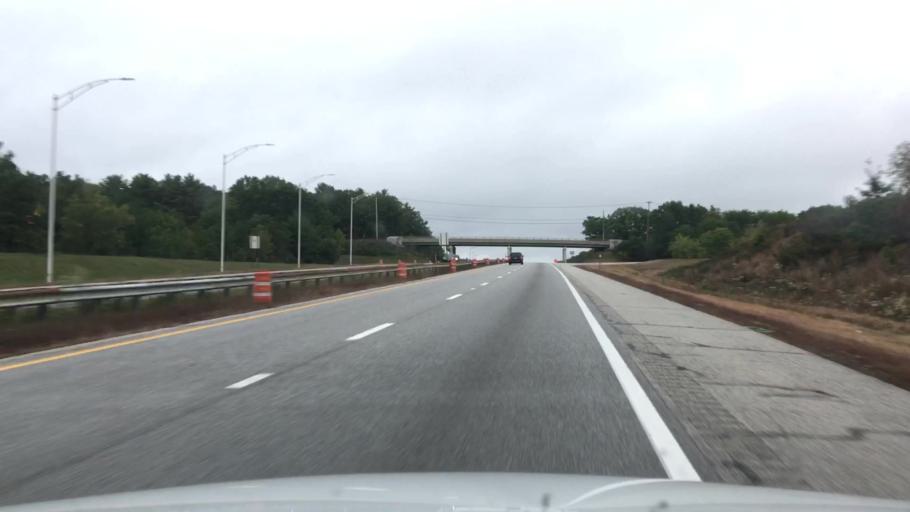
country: US
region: Maine
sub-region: Cumberland County
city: Cumberland Center
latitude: 43.8120
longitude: -70.3172
